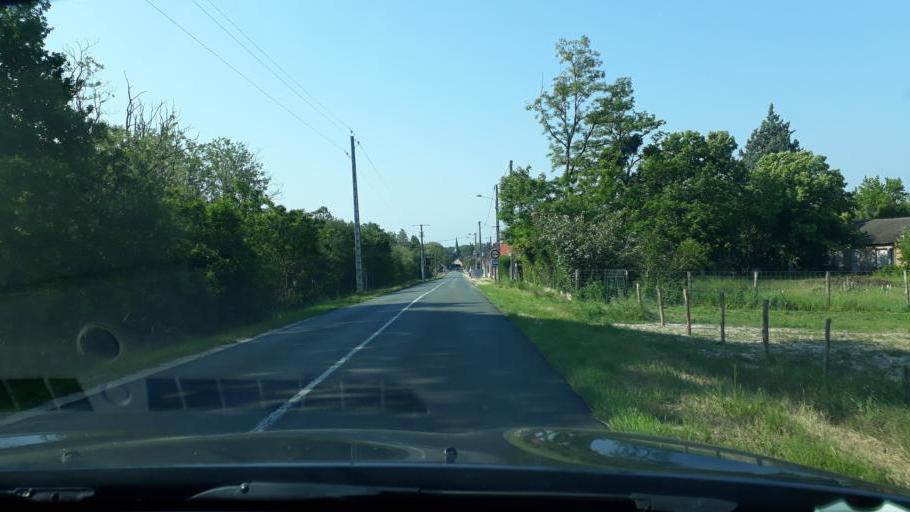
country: FR
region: Centre
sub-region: Departement du Loiret
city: Ligny-le-Ribault
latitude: 47.6898
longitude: 1.7849
